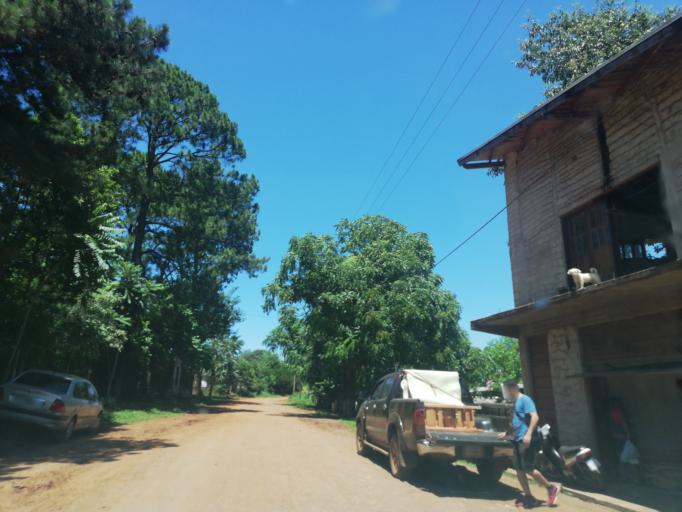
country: AR
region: Misiones
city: Garupa
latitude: -27.4504
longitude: -55.9026
